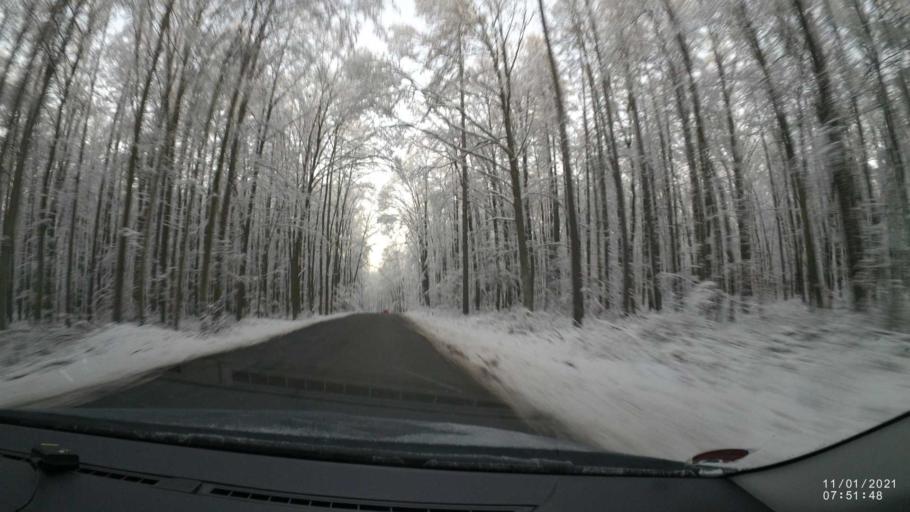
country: CZ
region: South Moravian
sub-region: Okres Blansko
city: Adamov
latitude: 49.2859
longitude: 16.6521
